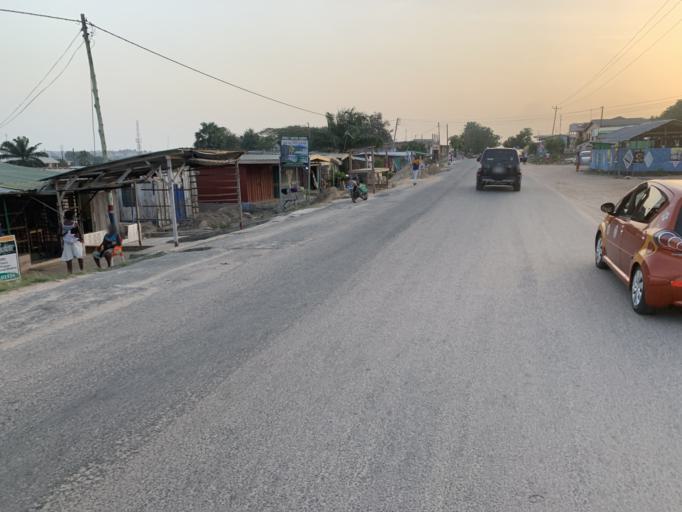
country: GH
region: Central
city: Winneba
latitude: 5.3539
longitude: -0.6156
